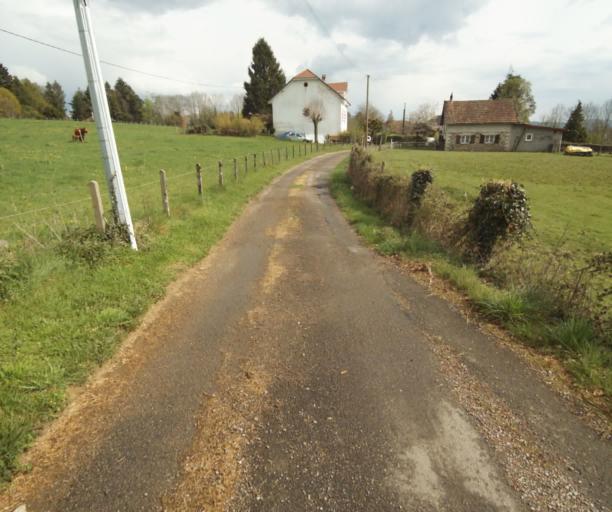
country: FR
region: Limousin
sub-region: Departement de la Correze
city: Tulle
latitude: 45.2895
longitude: 1.7391
